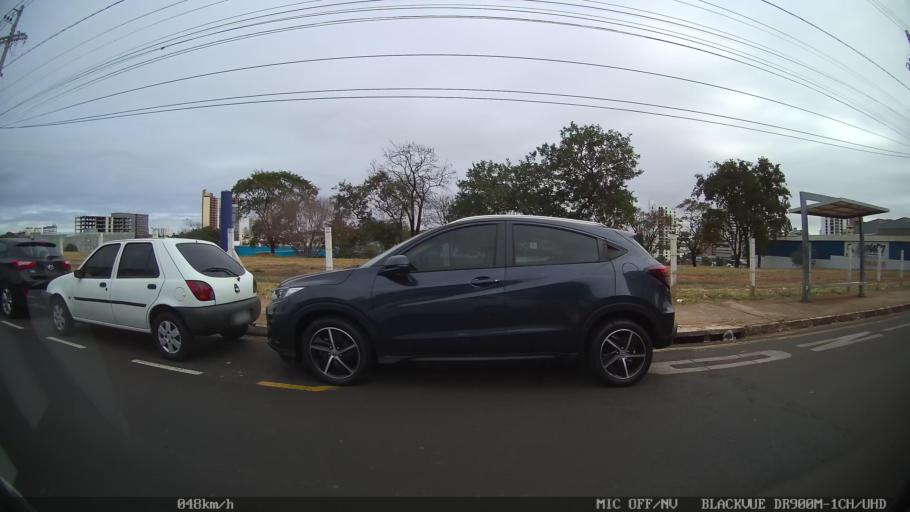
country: BR
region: Sao Paulo
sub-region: Sao Jose Do Rio Preto
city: Sao Jose do Rio Preto
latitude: -20.8251
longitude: -49.3828
